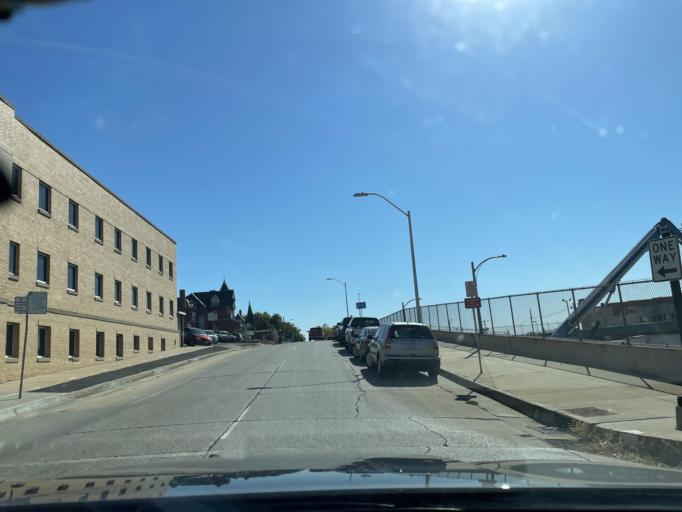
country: US
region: Missouri
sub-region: Buchanan County
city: Saint Joseph
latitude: 39.7658
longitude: -94.8495
